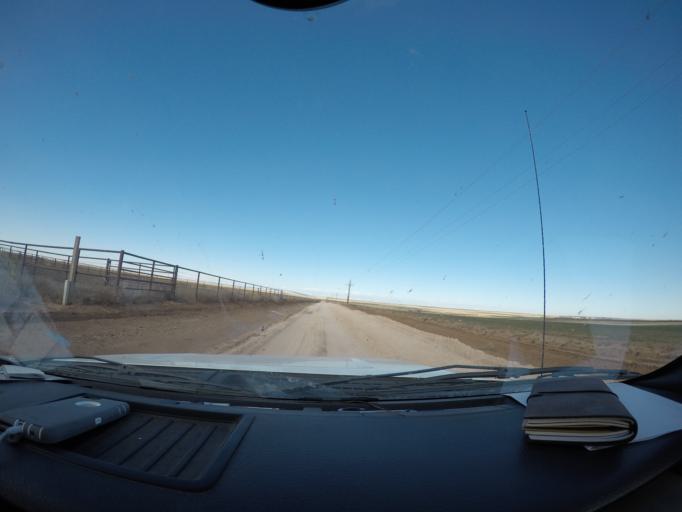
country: US
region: Texas
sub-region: Parmer County
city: Bovina
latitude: 34.6258
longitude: -103.0911
